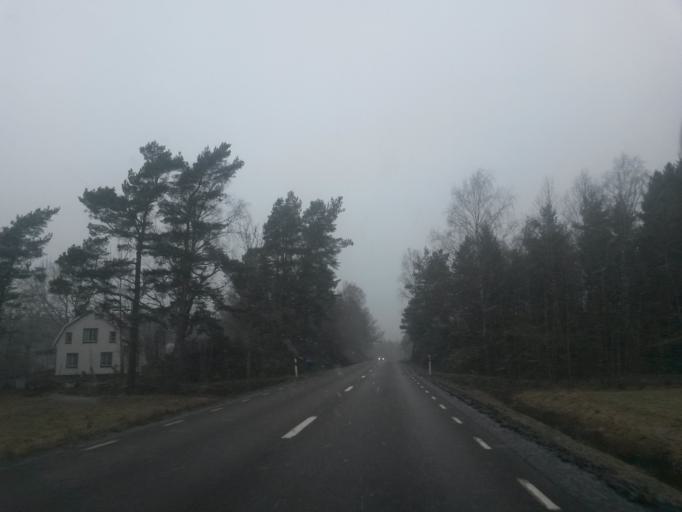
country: SE
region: Vaestra Goetaland
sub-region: Vanersborgs Kommun
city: Vargon
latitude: 58.2311
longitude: 12.4217
